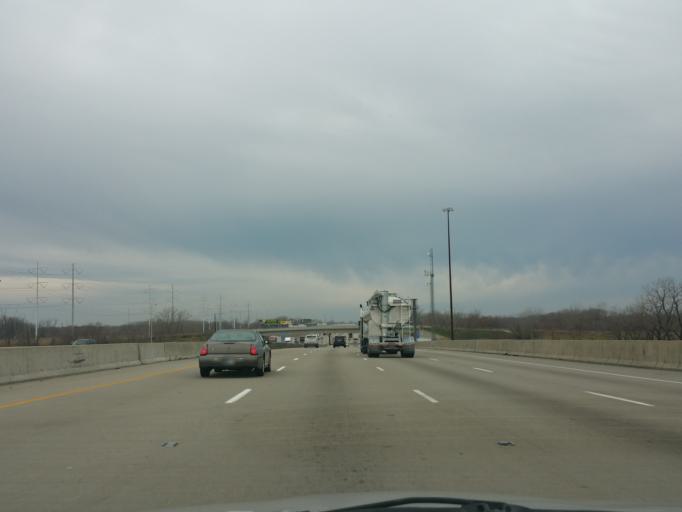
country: US
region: Indiana
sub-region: Lake County
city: New Chicago
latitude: 41.5675
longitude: -87.3138
